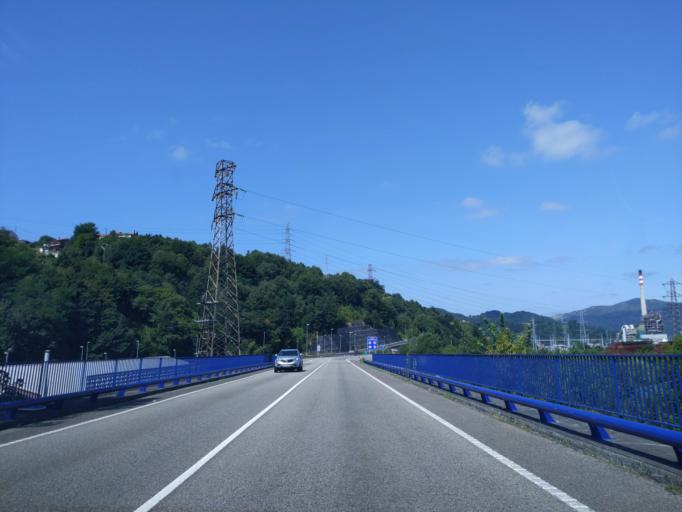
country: ES
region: Asturias
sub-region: Province of Asturias
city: Sama
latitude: 43.2995
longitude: -5.6883
